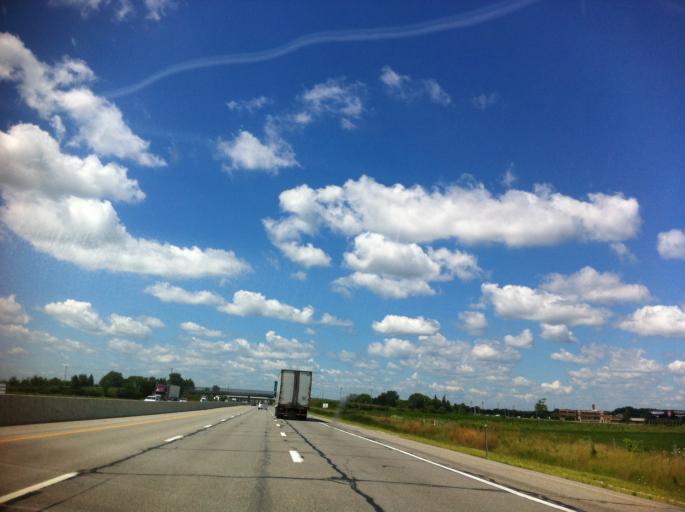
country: US
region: Ohio
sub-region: Wood County
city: Rossford
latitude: 41.5601
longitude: -83.5632
